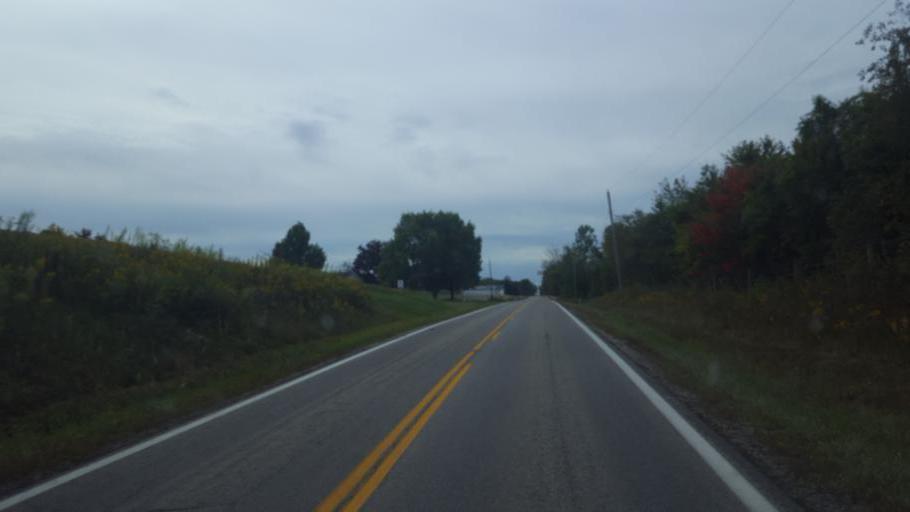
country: US
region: Ohio
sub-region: Knox County
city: Centerburg
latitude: 40.4454
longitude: -82.6976
